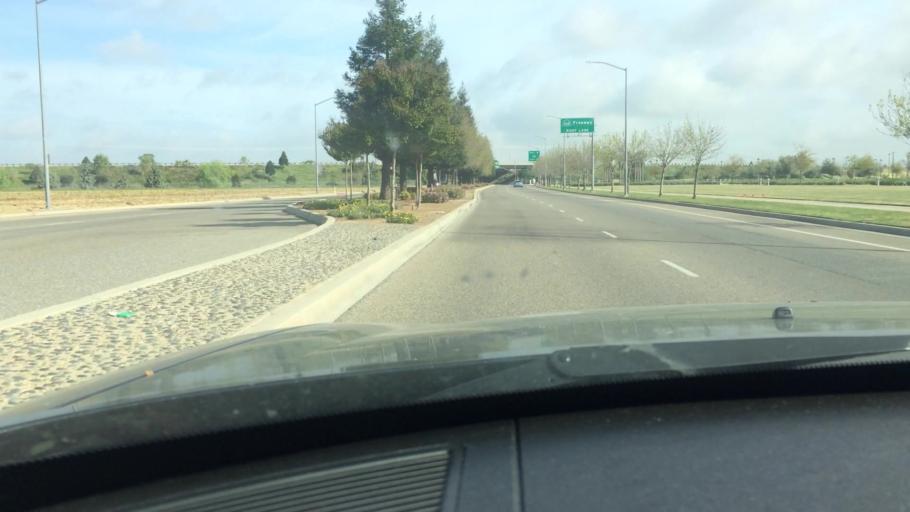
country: US
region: California
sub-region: Fresno County
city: Clovis
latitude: 36.8398
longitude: -119.6639
